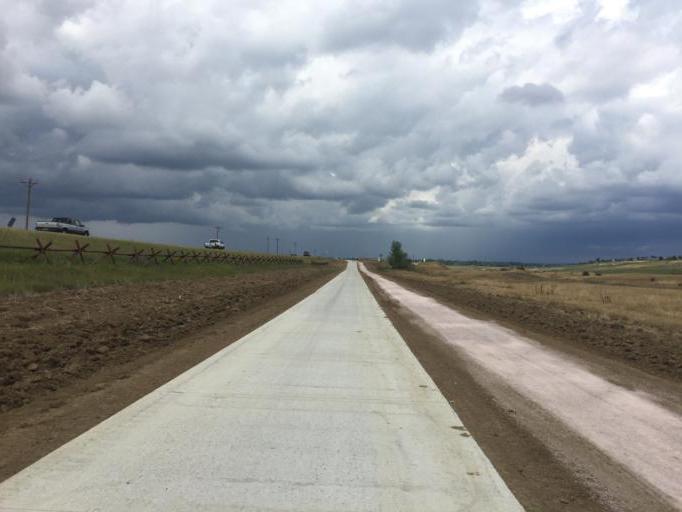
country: US
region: Colorado
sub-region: Larimer County
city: Loveland
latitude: 40.4775
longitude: -105.0961
